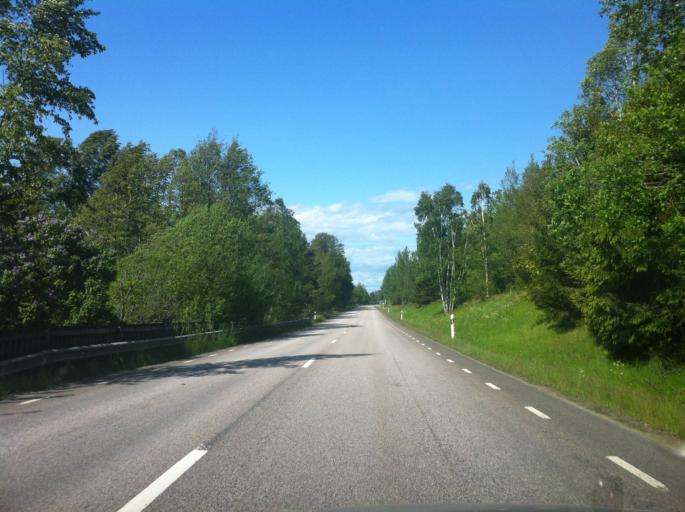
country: SE
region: Vaestra Goetaland
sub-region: Gullspangs Kommun
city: Gullspang
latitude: 59.0435
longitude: 14.1374
